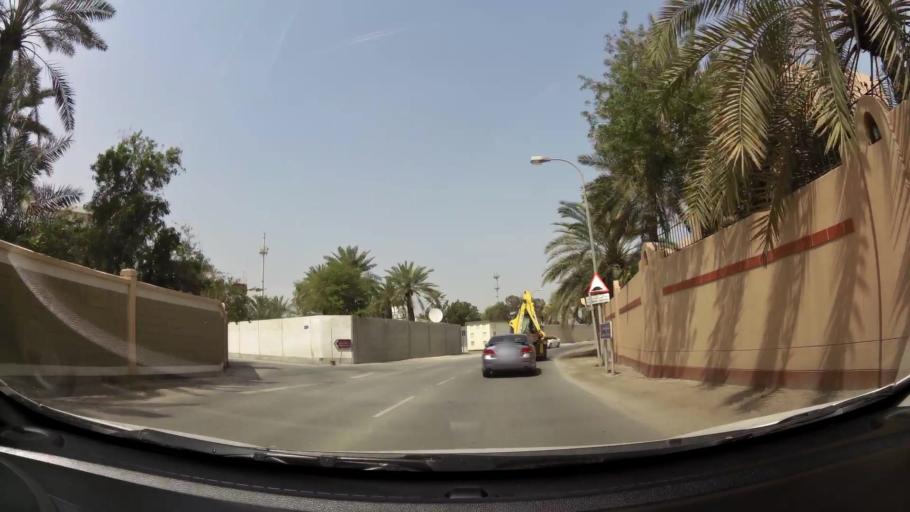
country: BH
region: Manama
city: Jidd Hafs
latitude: 26.2251
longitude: 50.4954
